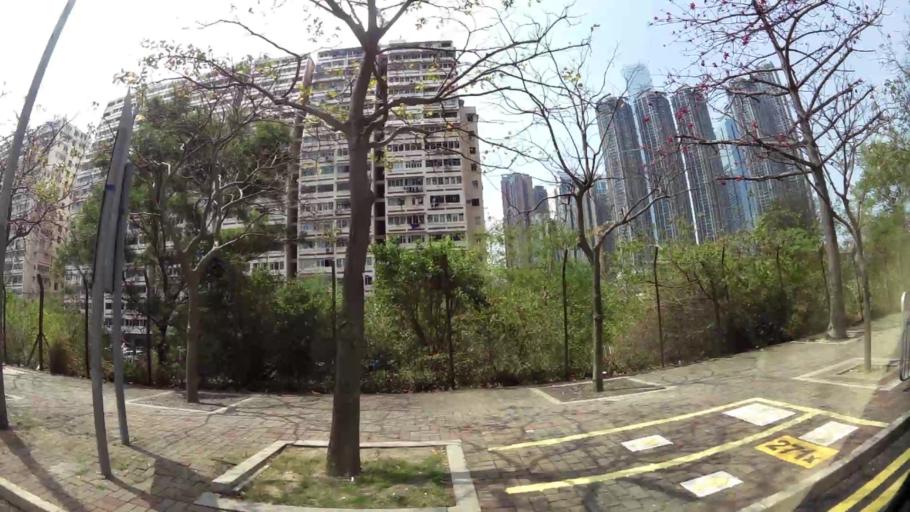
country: HK
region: Kowloon City
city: Kowloon
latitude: 22.3089
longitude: 114.1658
